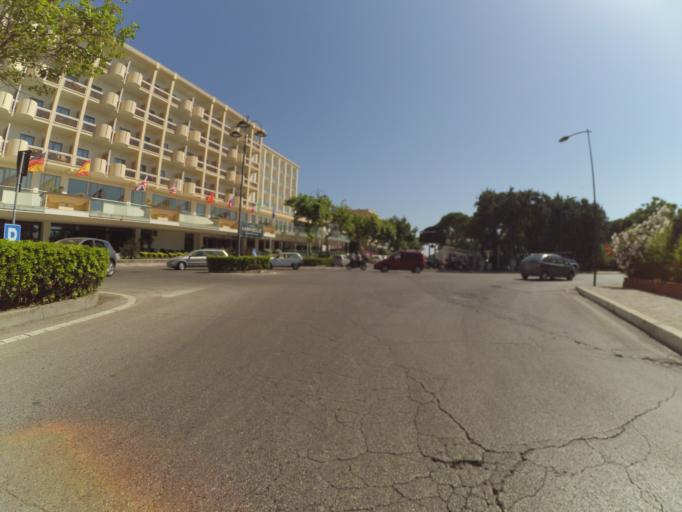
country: IT
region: Latium
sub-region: Provincia di Latina
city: Gaeta
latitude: 41.2108
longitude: 13.5714
